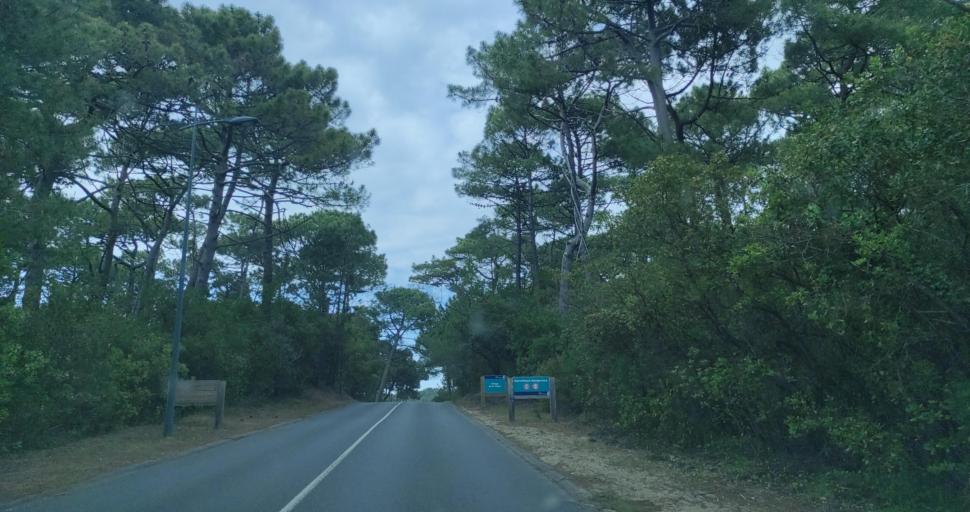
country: FR
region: Aquitaine
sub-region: Departement de la Gironde
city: Arcachon
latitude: 44.6642
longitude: -1.2432
